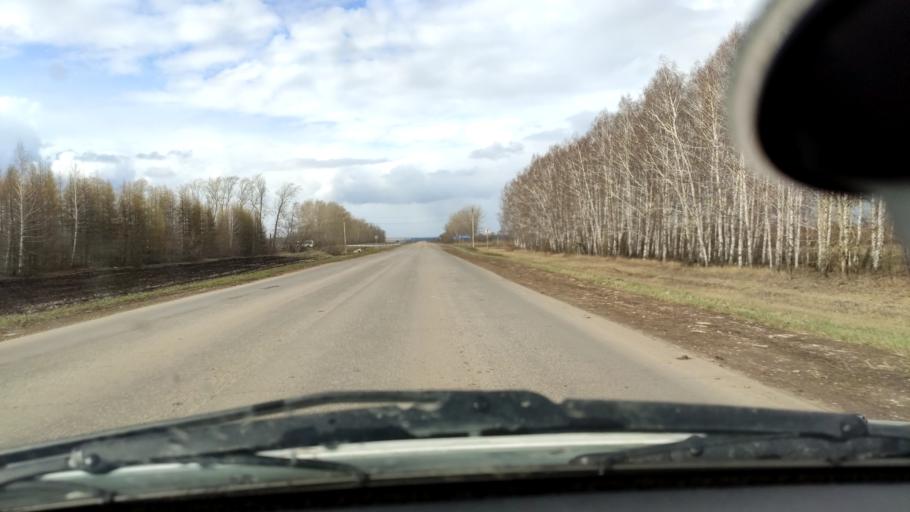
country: RU
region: Bashkortostan
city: Buzdyak
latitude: 54.7063
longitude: 54.5653
